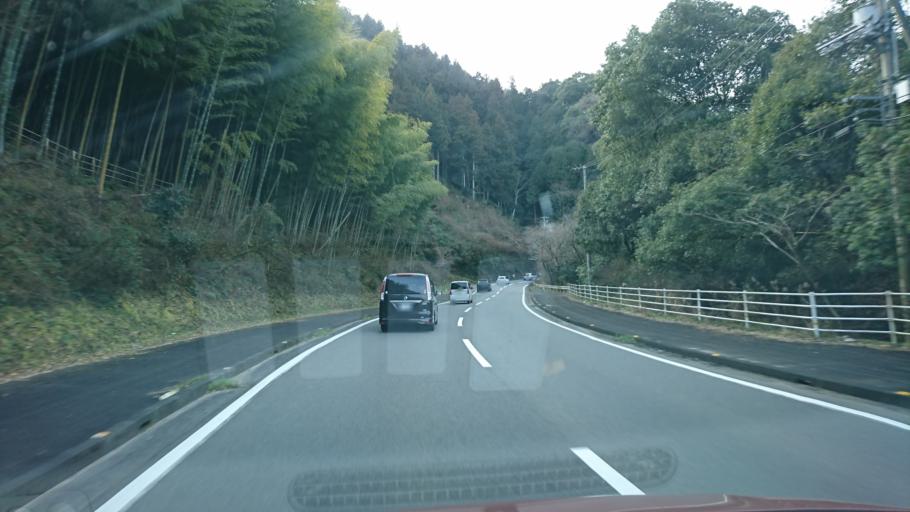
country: JP
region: Ehime
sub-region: Shikoku-chuo Shi
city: Matsuyama
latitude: 33.8968
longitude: 132.8583
